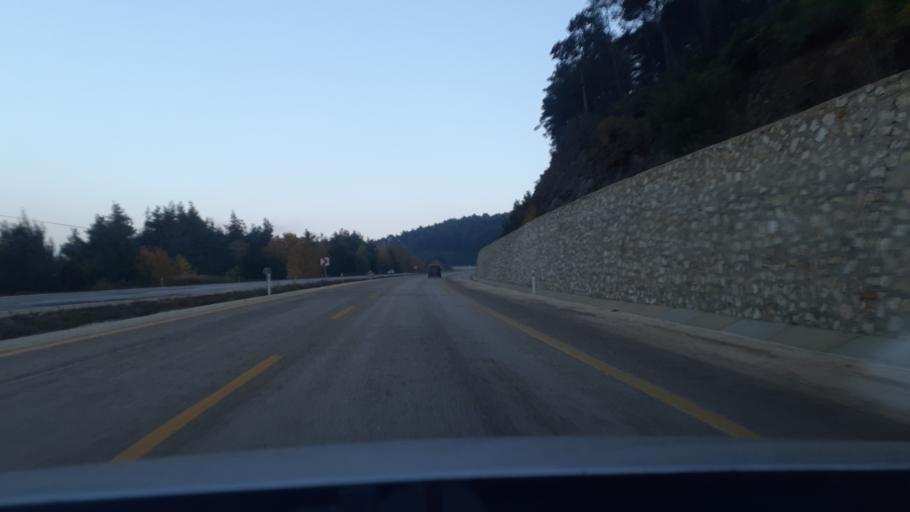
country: TR
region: Hatay
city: Yayladagi
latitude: 35.8940
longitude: 36.0830
